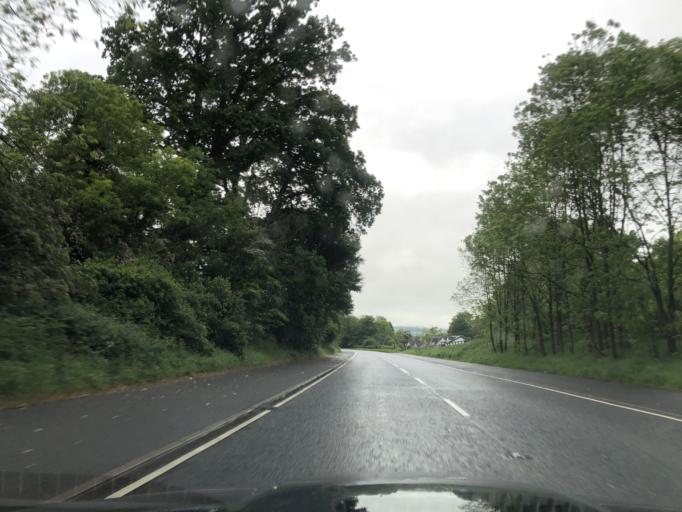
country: GB
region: Northern Ireland
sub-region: Antrim Borough
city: Antrim
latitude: 54.6992
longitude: -6.2235
